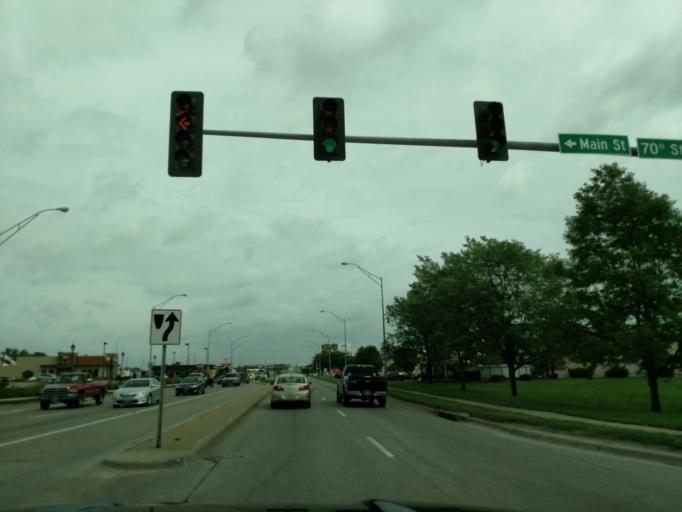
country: US
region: Nebraska
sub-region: Douglas County
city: Ralston
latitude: 41.2021
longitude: -96.0238
